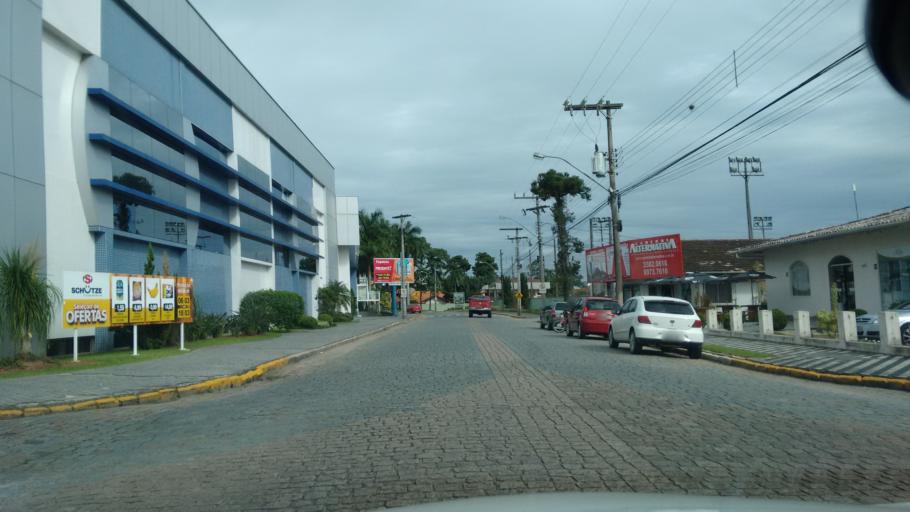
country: BR
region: Santa Catarina
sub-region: Timbo
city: Timbo
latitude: -26.8273
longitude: -49.2718
